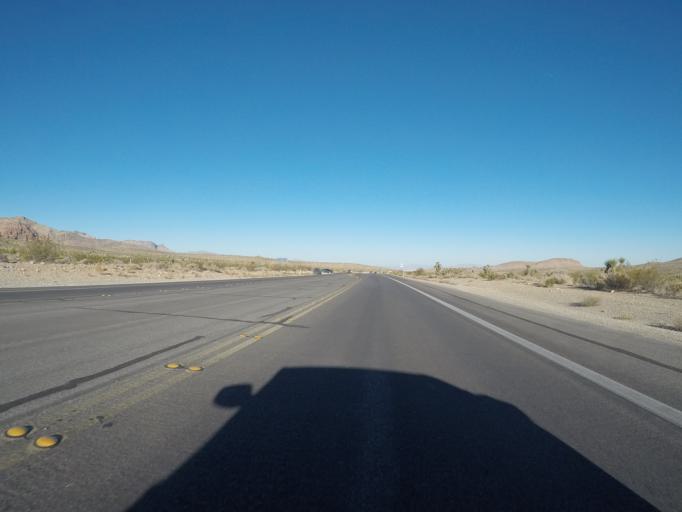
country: US
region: Nevada
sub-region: Clark County
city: Summerlin South
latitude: 36.1305
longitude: -115.4235
